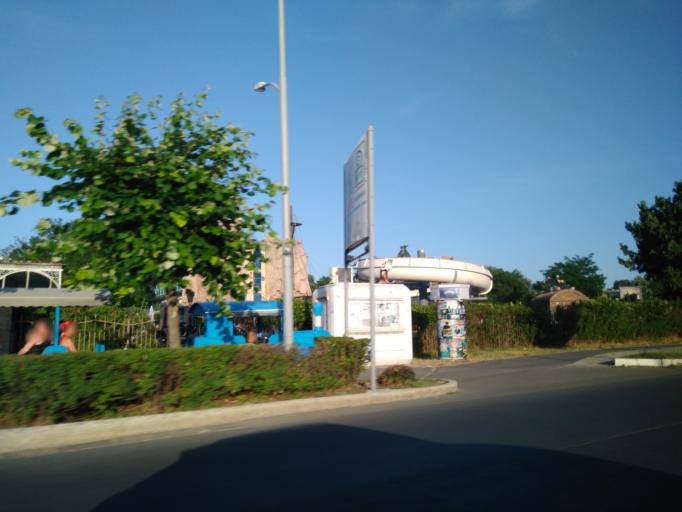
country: BG
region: Burgas
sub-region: Obshtina Nesebur
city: Nesebar
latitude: 42.6662
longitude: 27.7069
